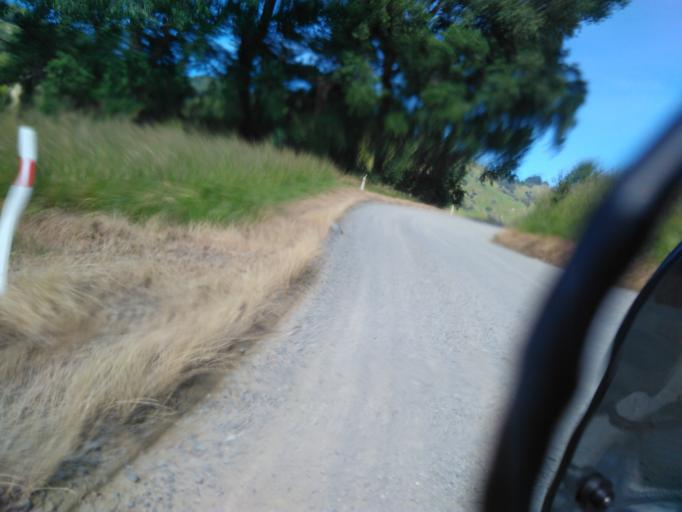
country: NZ
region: Hawke's Bay
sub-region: Wairoa District
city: Wairoa
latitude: -38.8694
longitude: 177.2041
